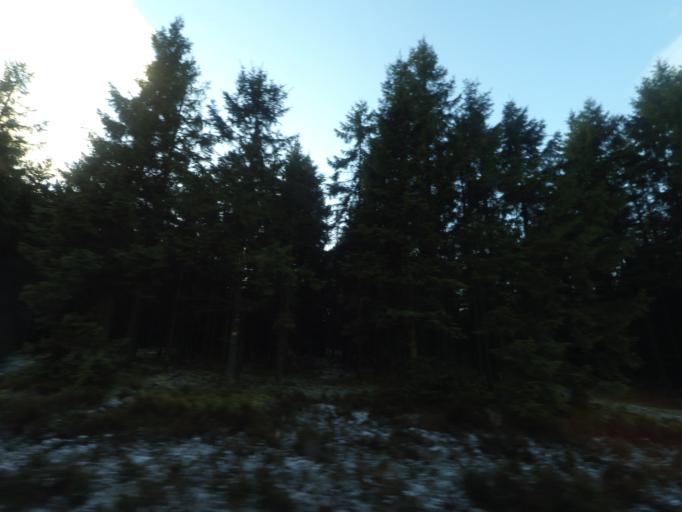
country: DK
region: Central Jutland
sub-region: Ikast-Brande Kommune
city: Brande
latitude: 56.0122
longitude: 9.1640
